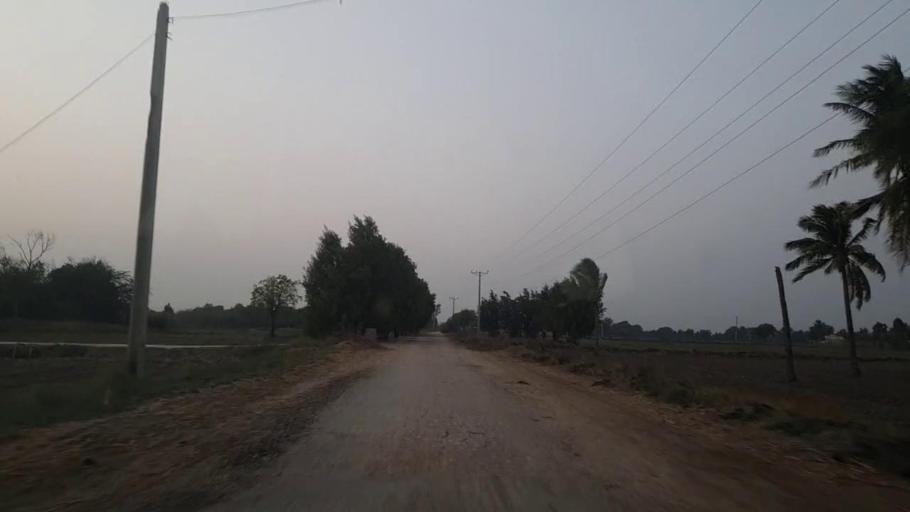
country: PK
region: Sindh
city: Mirpur Sakro
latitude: 24.5916
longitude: 67.7797
